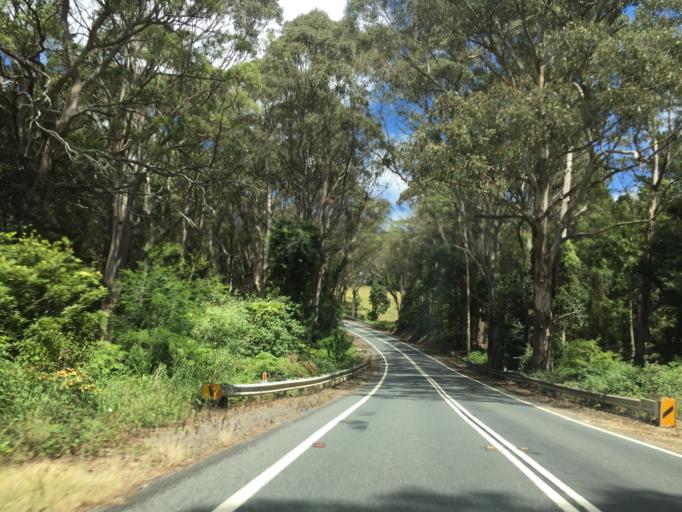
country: AU
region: New South Wales
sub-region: Blue Mountains Municipality
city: Hazelbrook
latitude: -33.5080
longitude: 150.4964
